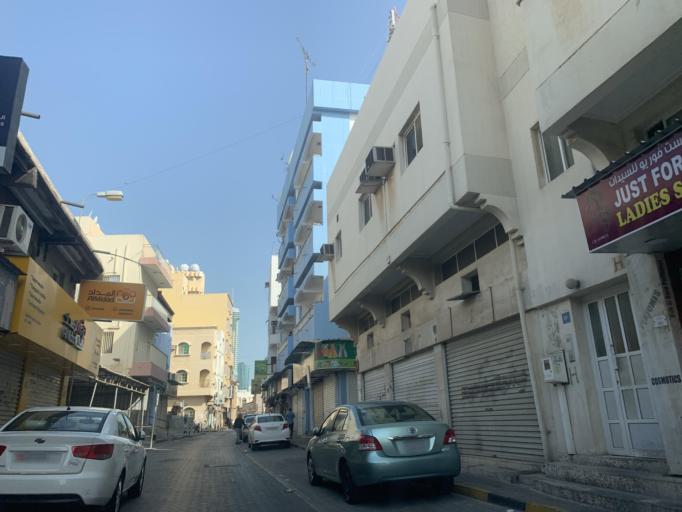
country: BH
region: Manama
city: Manama
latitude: 26.2290
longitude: 50.5781
